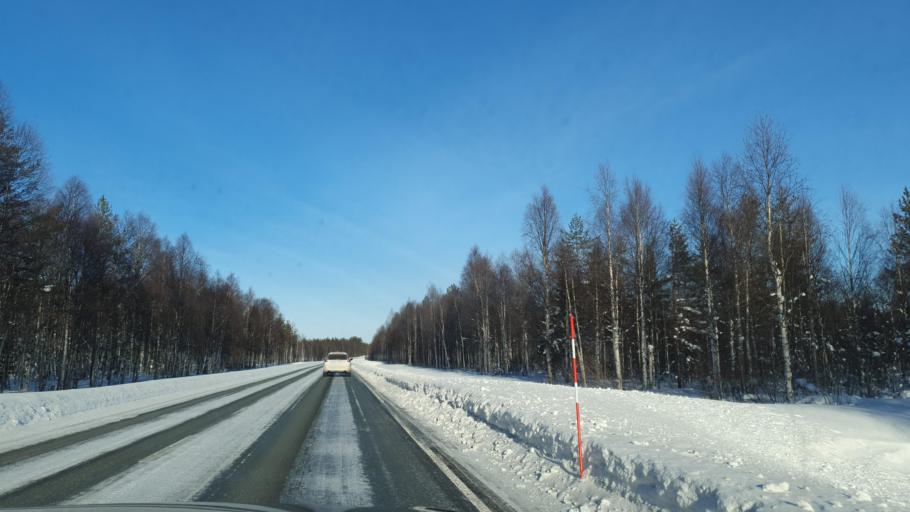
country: SE
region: Norrbotten
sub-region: Overtornea Kommun
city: OEvertornea
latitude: 66.4494
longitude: 23.6935
